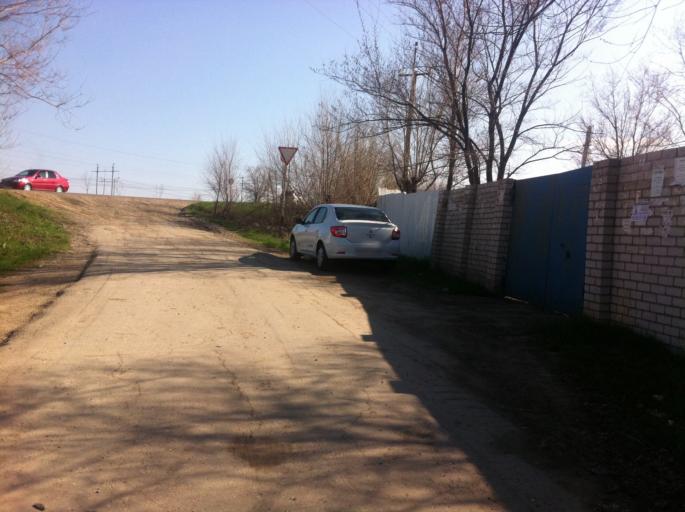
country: RU
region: Samara
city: Smyshlyayevka
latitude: 53.1195
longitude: 50.4162
